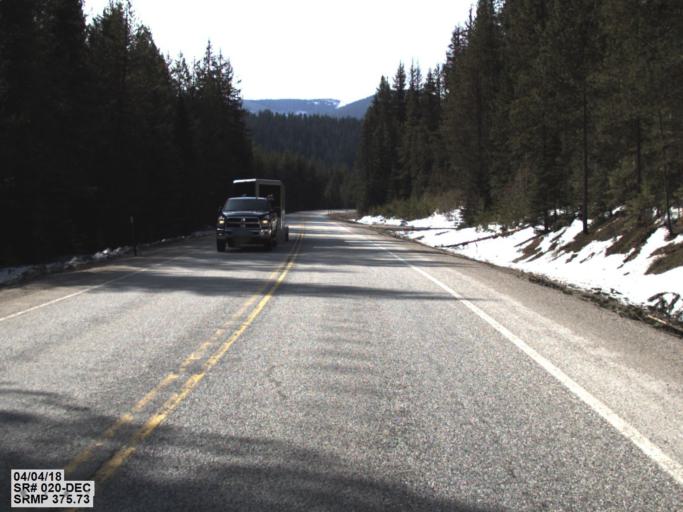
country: US
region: Washington
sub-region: Stevens County
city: Chewelah
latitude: 48.5657
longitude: -117.5558
